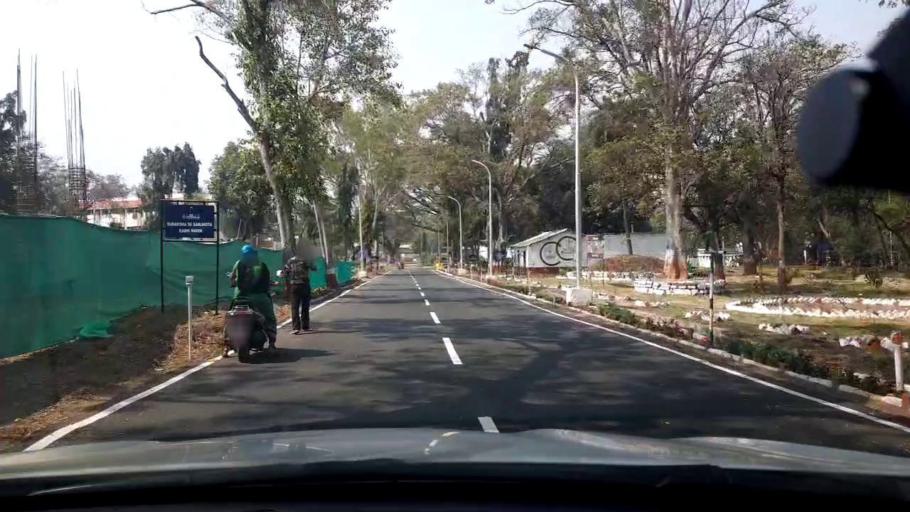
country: IN
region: Maharashtra
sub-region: Pune Division
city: Khadki
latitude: 18.5530
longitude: 73.8677
